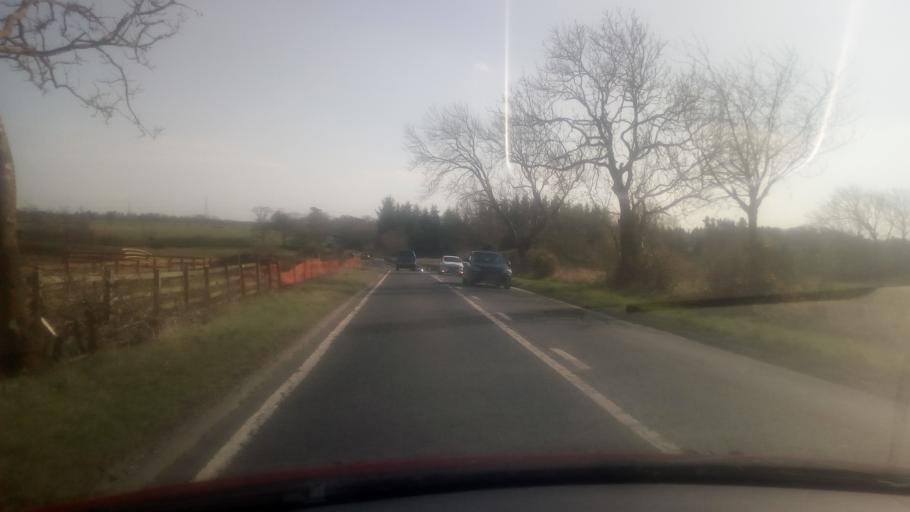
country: GB
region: England
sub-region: Northumberland
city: Darras Hall
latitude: 55.0656
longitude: -1.7830
